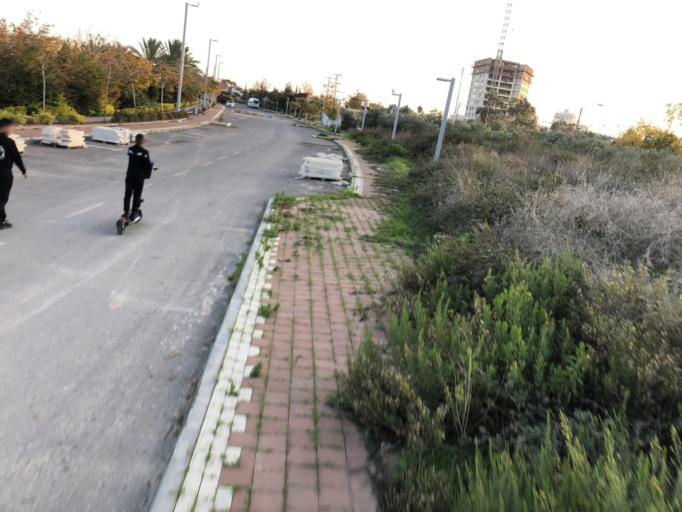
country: IL
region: Northern District
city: `Akko
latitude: 32.9317
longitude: 35.0825
